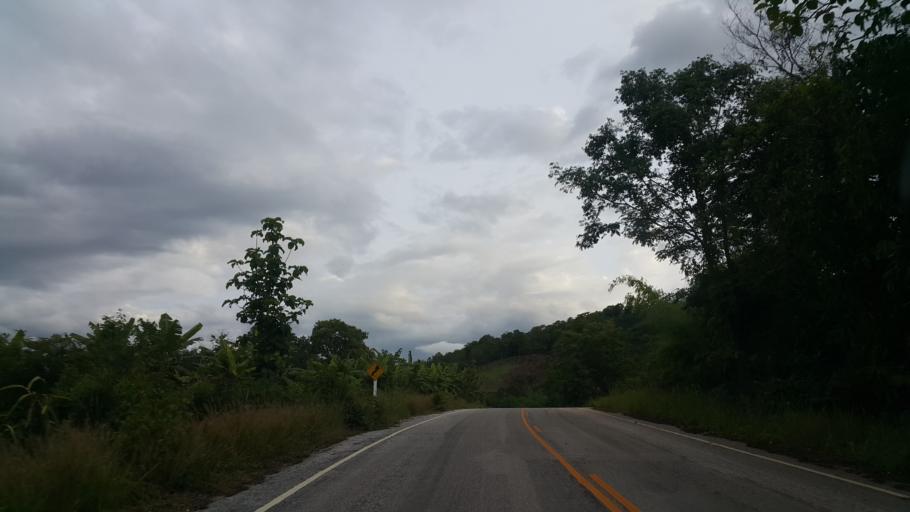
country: TH
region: Loei
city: Na Haeo
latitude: 17.4809
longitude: 101.1084
